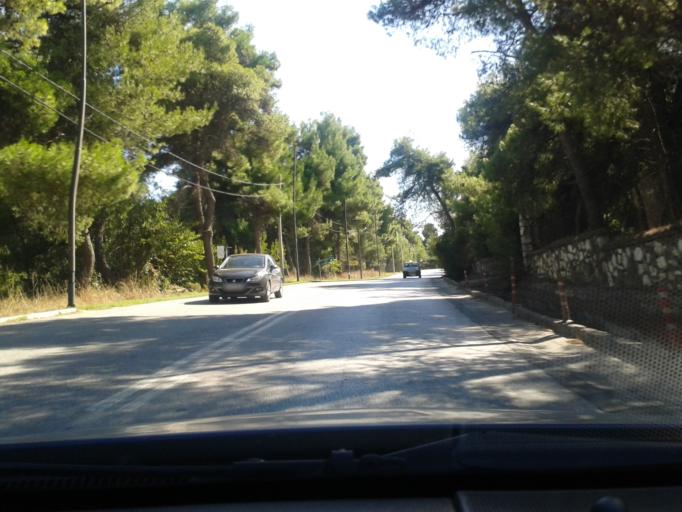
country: GR
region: Attica
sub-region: Nomarchia Anatolikis Attikis
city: Dionysos
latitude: 38.1036
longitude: 23.8736
